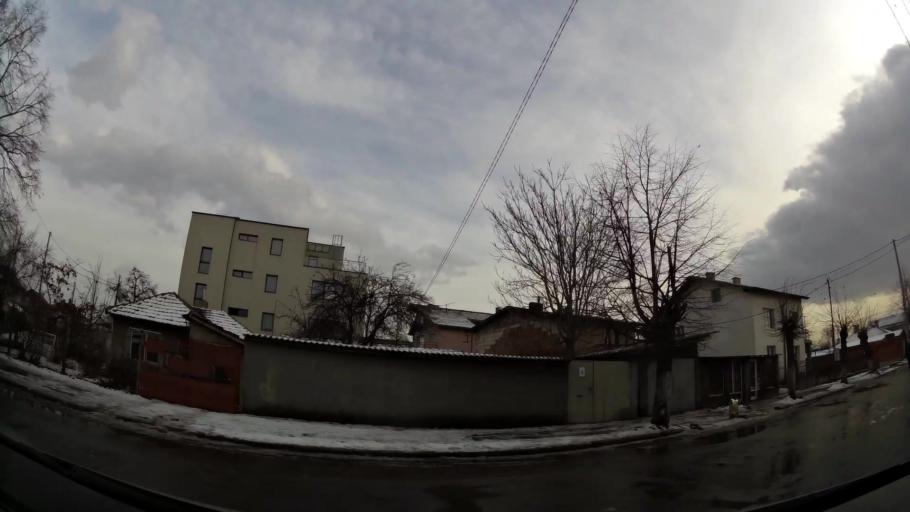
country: BG
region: Sofia-Capital
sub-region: Stolichna Obshtina
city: Sofia
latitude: 42.6890
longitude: 23.3831
